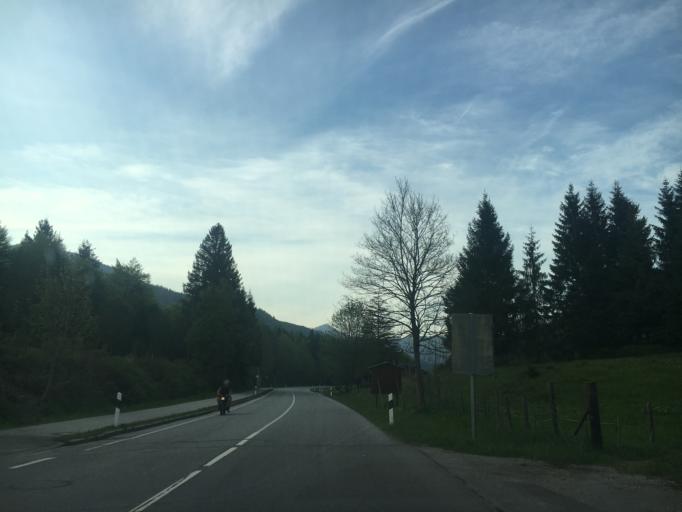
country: DE
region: Bavaria
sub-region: Upper Bavaria
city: Wallgau
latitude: 47.5291
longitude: 11.2842
